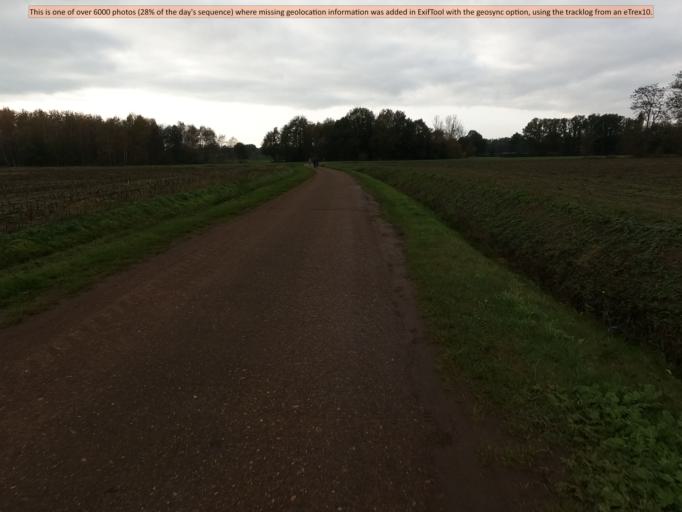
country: BE
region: Flanders
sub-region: Provincie Antwerpen
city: Berlaar
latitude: 51.1311
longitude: 4.6823
